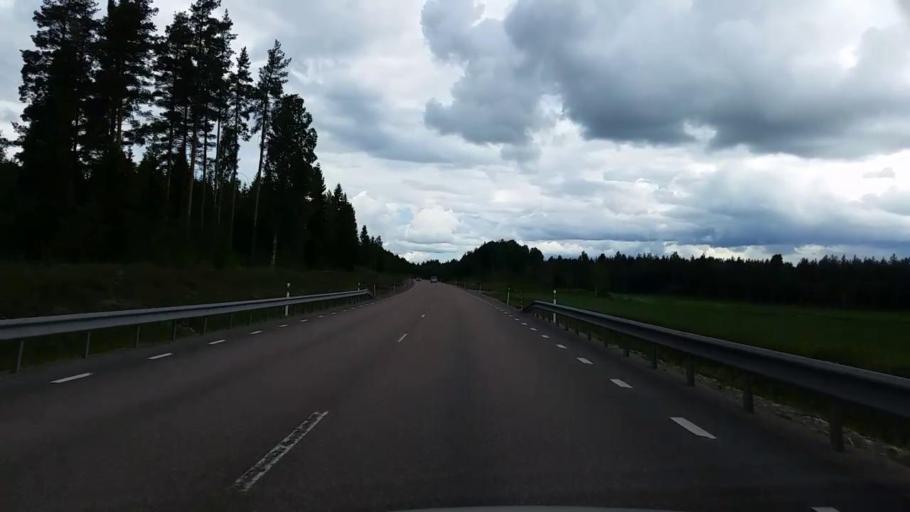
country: SE
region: Gaevleborg
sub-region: Hofors Kommun
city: Hofors
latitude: 60.4751
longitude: 16.4474
